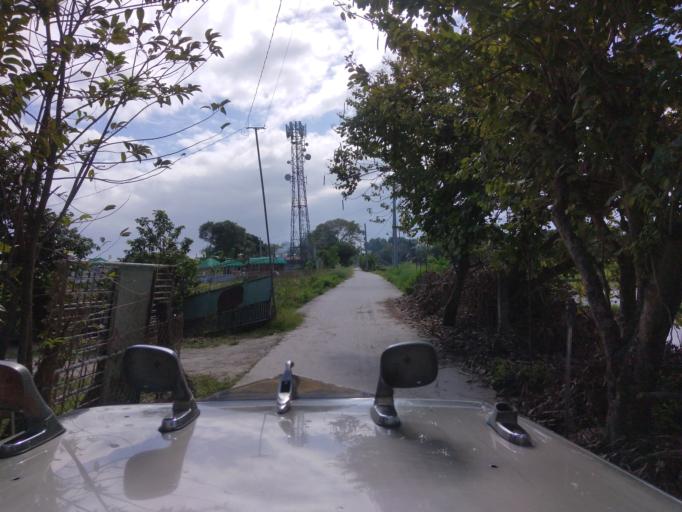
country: PH
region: Central Luzon
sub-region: Province of Pampanga
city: San Patricio
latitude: 15.0900
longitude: 120.7154
